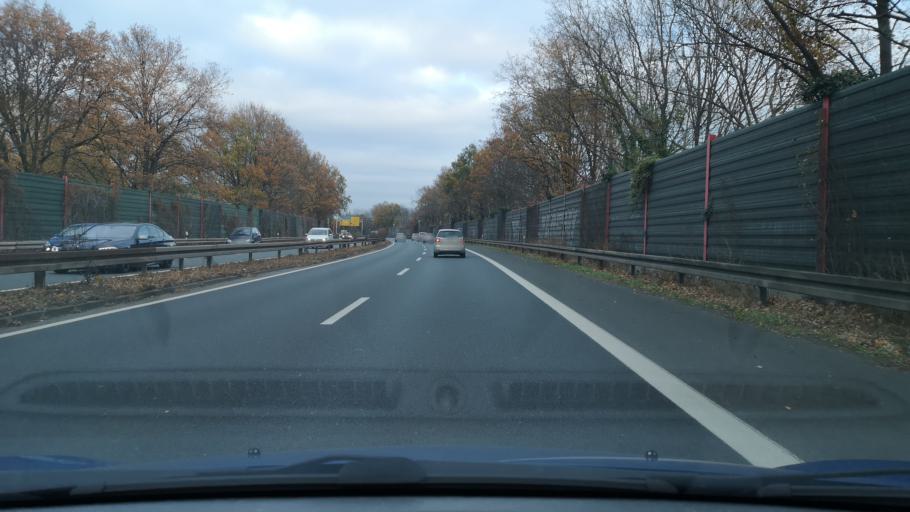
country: DE
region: Lower Saxony
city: Isernhagen Farster Bauerschaft
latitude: 52.3989
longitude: 9.8105
